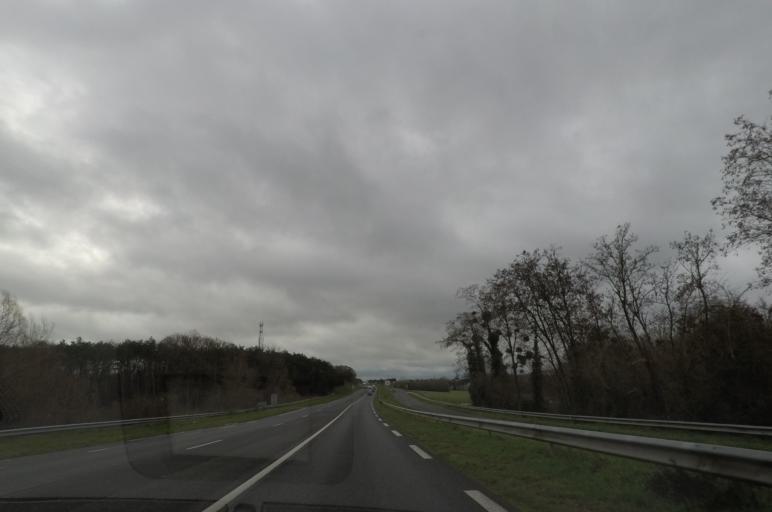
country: FR
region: Centre
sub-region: Departement du Loir-et-Cher
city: Saint-Sulpice-de-Pommeray
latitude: 47.6538
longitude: 1.2717
